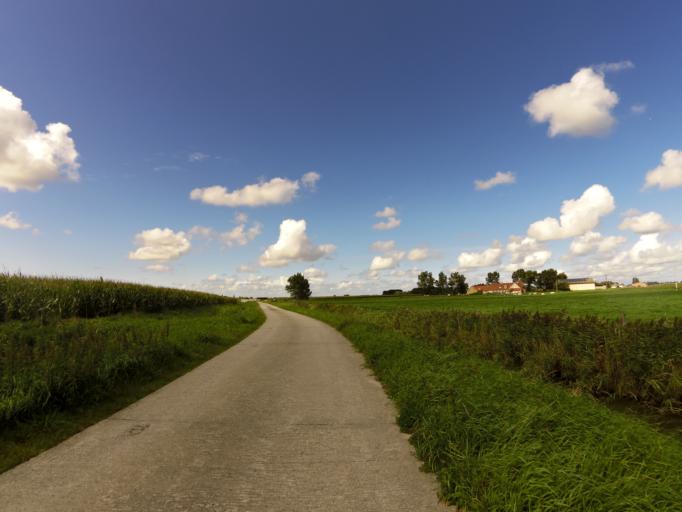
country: BE
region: Flanders
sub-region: Provincie West-Vlaanderen
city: Middelkerke
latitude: 51.1523
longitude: 2.8778
